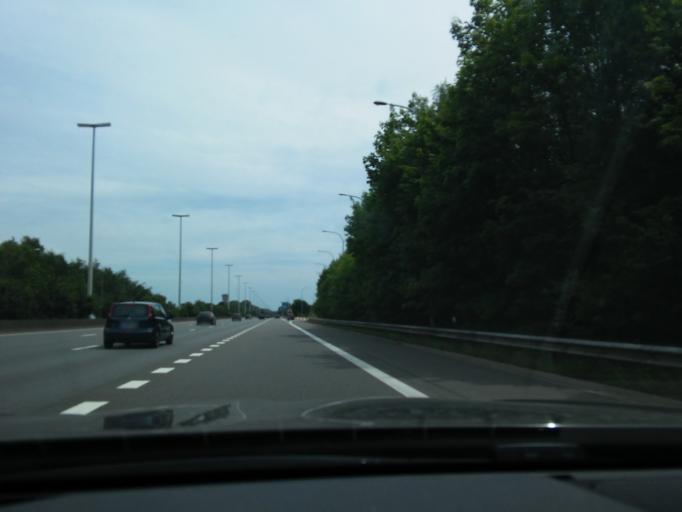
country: BE
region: Flanders
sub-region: Provincie Vlaams-Brabant
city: Leuven
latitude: 50.8451
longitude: 4.7101
